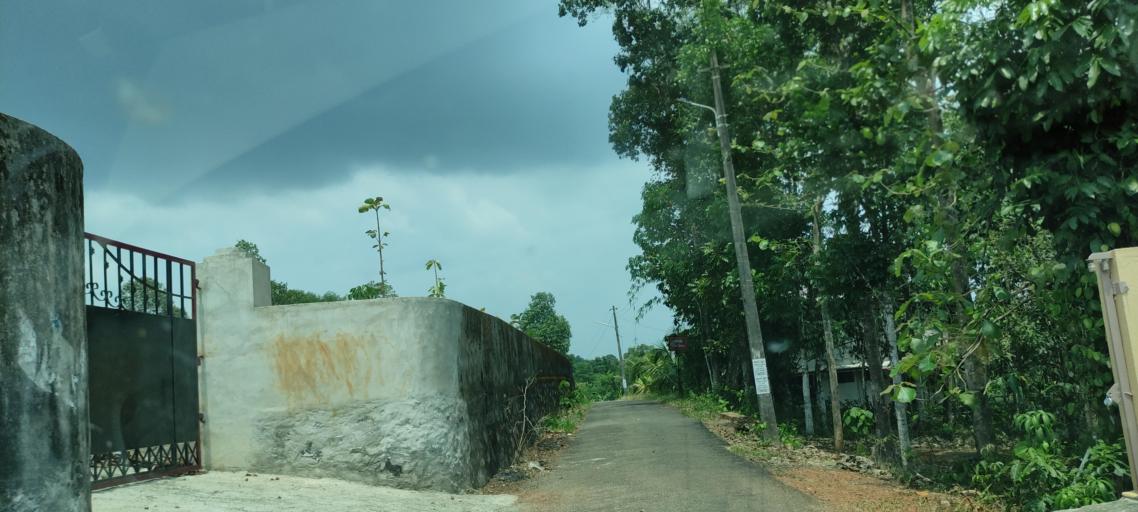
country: IN
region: Kerala
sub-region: Pattanamtitta
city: Adur
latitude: 9.1723
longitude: 76.7474
